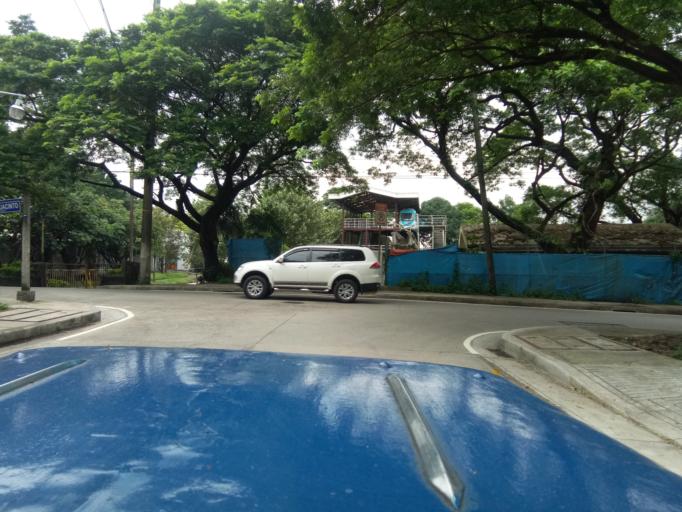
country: PH
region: Metro Manila
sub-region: Quezon City
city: Quezon City
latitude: 14.6529
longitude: 121.0628
